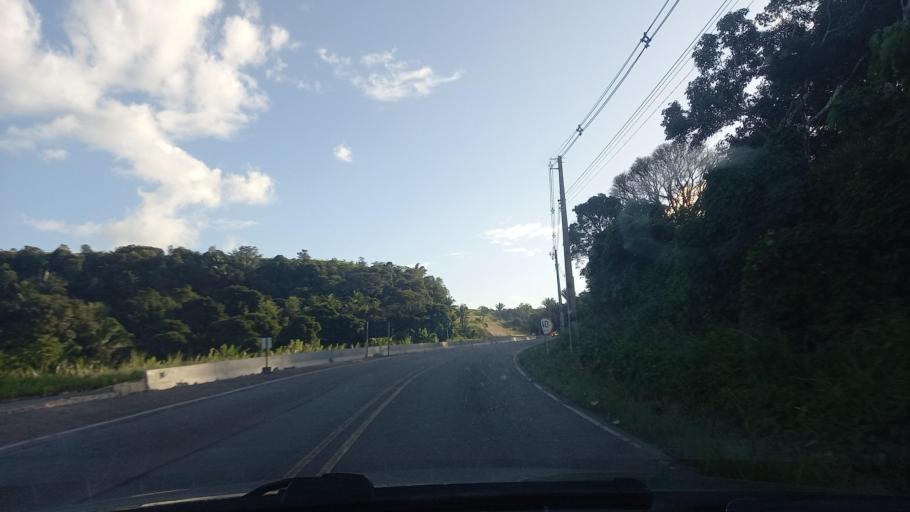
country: BR
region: Alagoas
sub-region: Sao Miguel Dos Campos
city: Sao Miguel dos Campos
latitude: -9.8208
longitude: -36.2210
